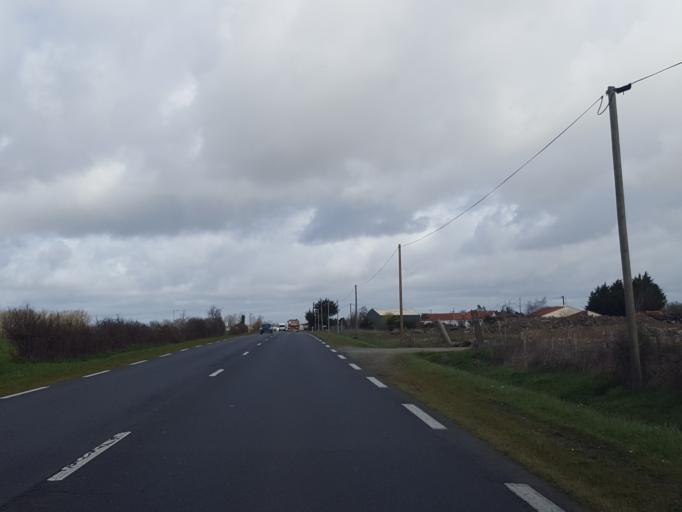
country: FR
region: Pays de la Loire
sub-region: Departement de la Loire-Atlantique
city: Les Sorinieres
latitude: 47.1041
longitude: -1.5359
